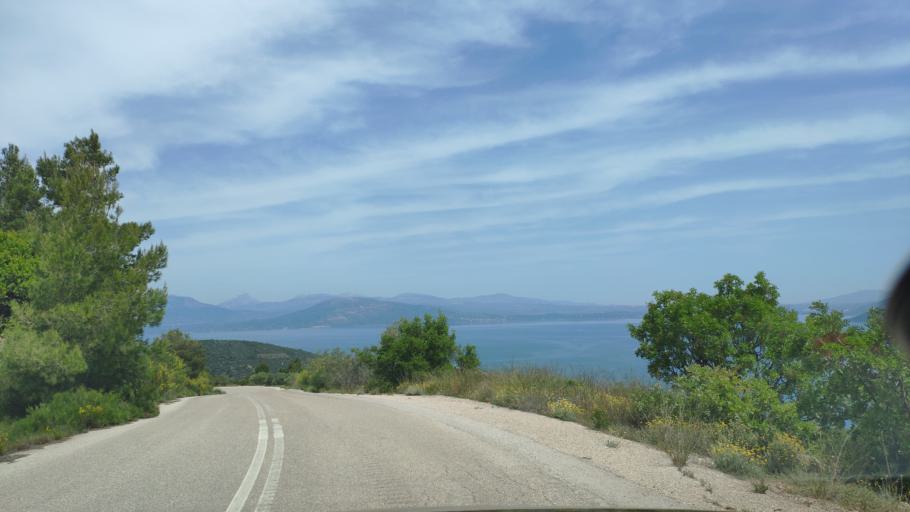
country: GR
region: Attica
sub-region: Nomarchia Anatolikis Attikis
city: Grammatiko
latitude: 38.2562
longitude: 23.9676
